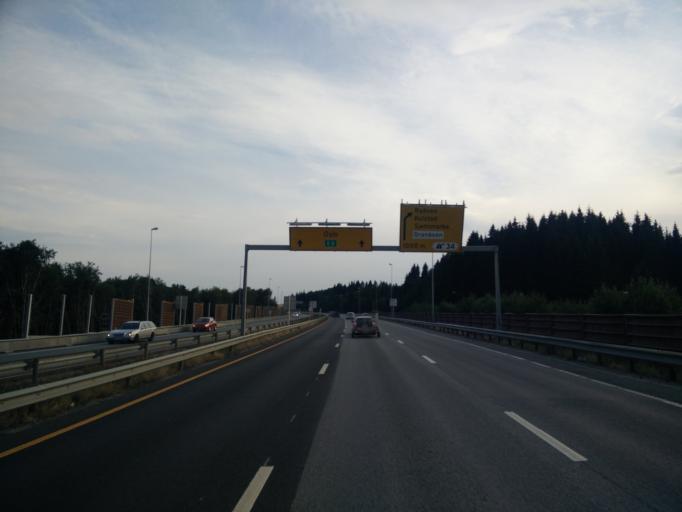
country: NO
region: Sor-Trondelag
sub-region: Trondheim
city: Trondheim
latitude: 63.3841
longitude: 10.3761
